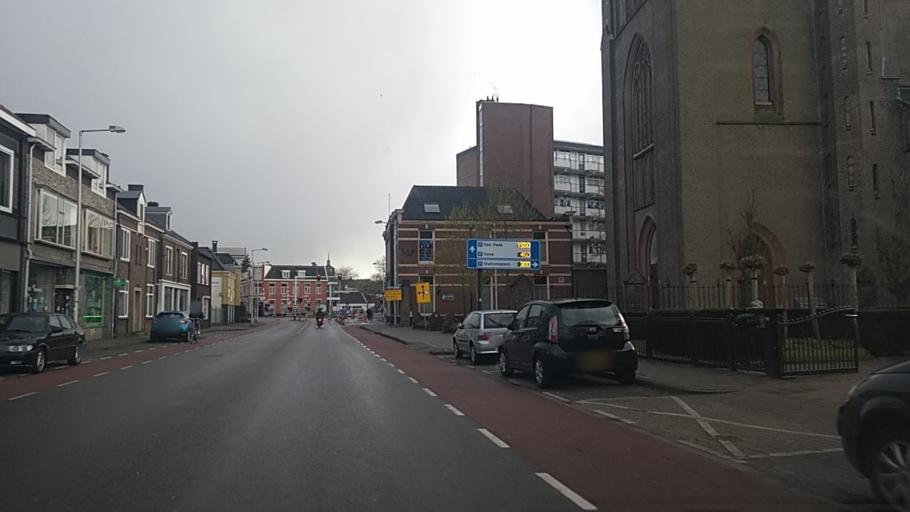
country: NL
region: Overijssel
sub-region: Gemeente Enschede
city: Enschede
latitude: 52.2246
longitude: 6.8996
